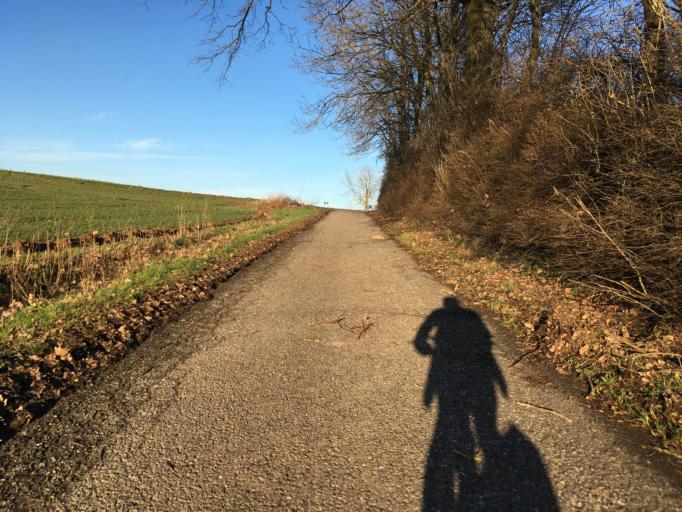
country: DE
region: Baden-Wuerttemberg
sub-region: Regierungsbezirk Stuttgart
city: Ittlingen
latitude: 49.1831
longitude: 8.9129
